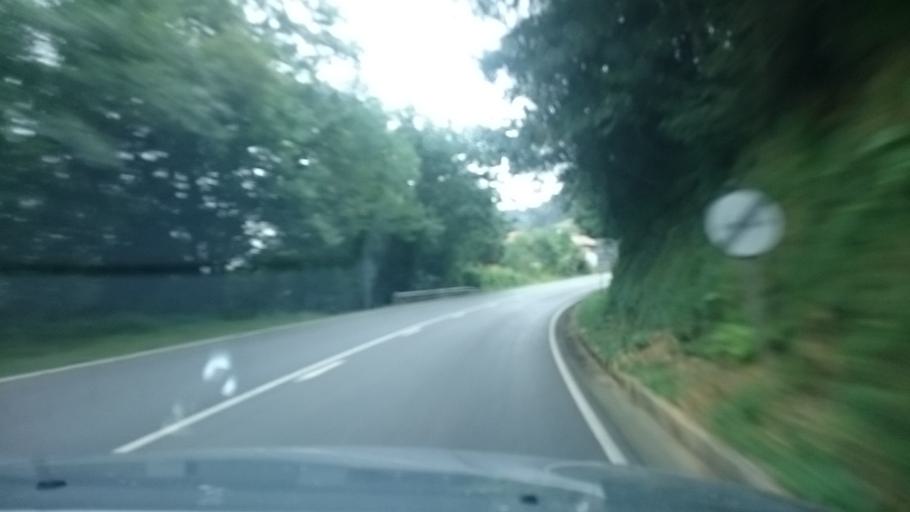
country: ES
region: Asturias
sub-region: Province of Asturias
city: Carrena
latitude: 43.4087
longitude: -4.8895
